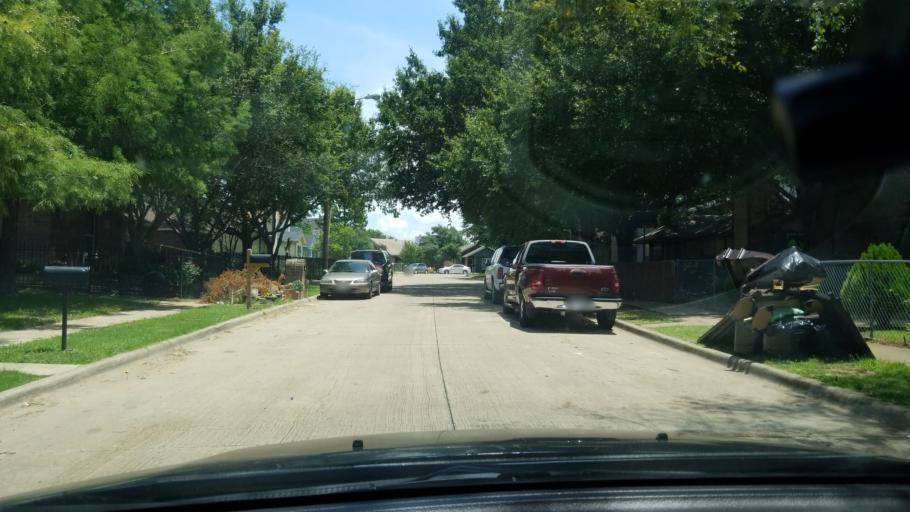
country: US
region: Texas
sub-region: Dallas County
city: Balch Springs
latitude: 32.7519
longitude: -96.6454
